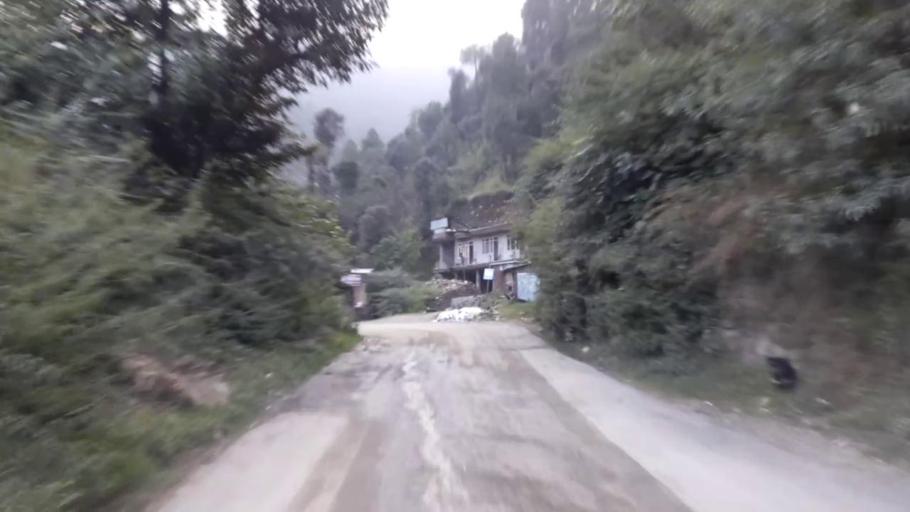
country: IN
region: Himachal Pradesh
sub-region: Shimla
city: Shimla
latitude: 31.0669
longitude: 77.1460
